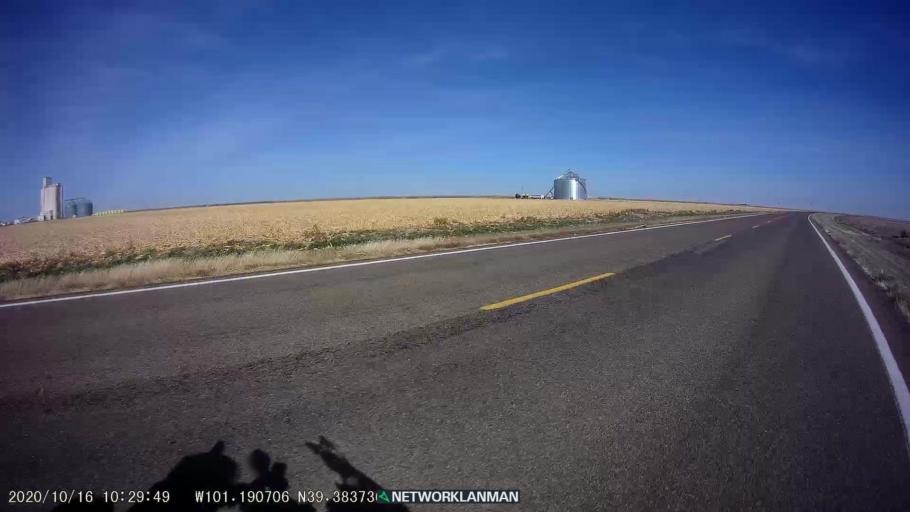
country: US
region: Kansas
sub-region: Thomas County
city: Colby
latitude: 39.3840
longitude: -101.1902
